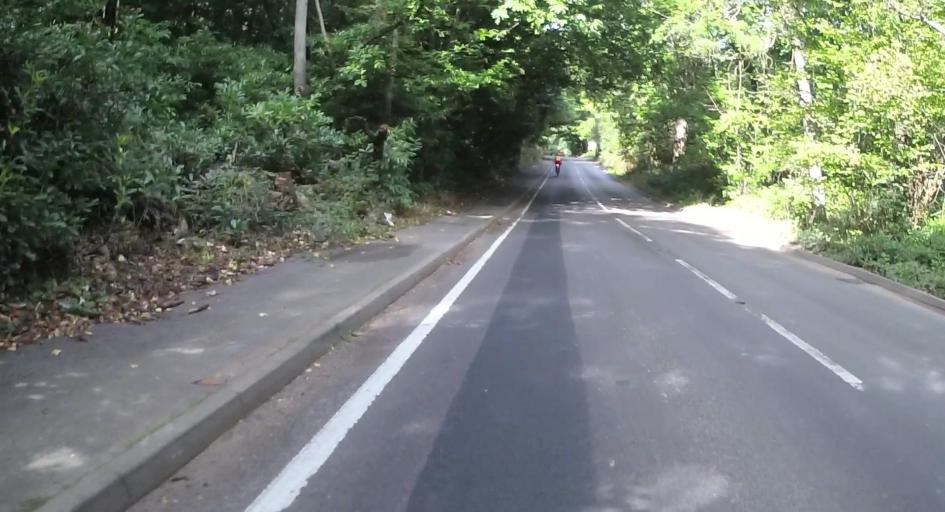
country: GB
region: England
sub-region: Surrey
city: Virginia Water
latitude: 51.3839
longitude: -0.5743
